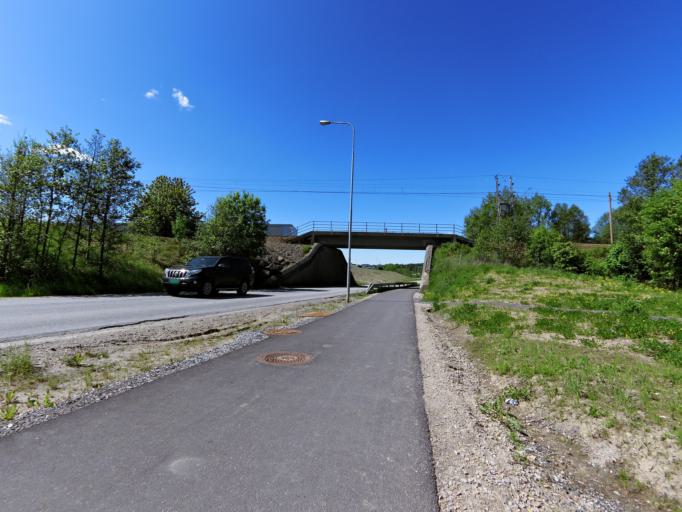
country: NO
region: Ostfold
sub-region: Fredrikstad
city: Fredrikstad
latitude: 59.2405
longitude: 10.9856
